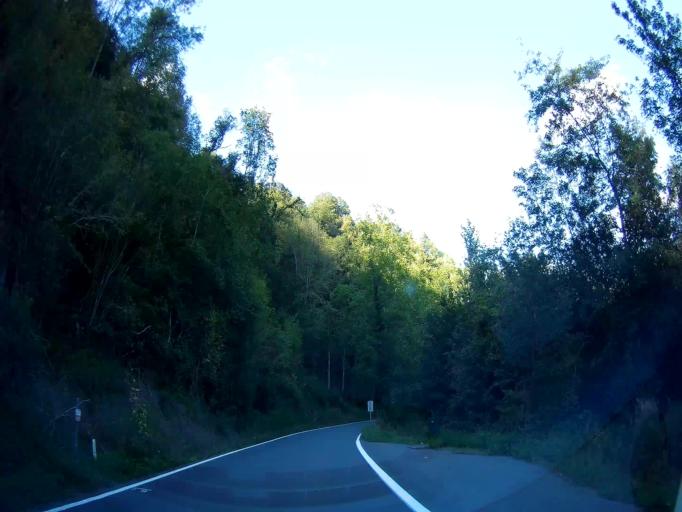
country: BE
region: Wallonia
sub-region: Province de Namur
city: Onhaye
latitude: 50.2975
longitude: 4.8143
